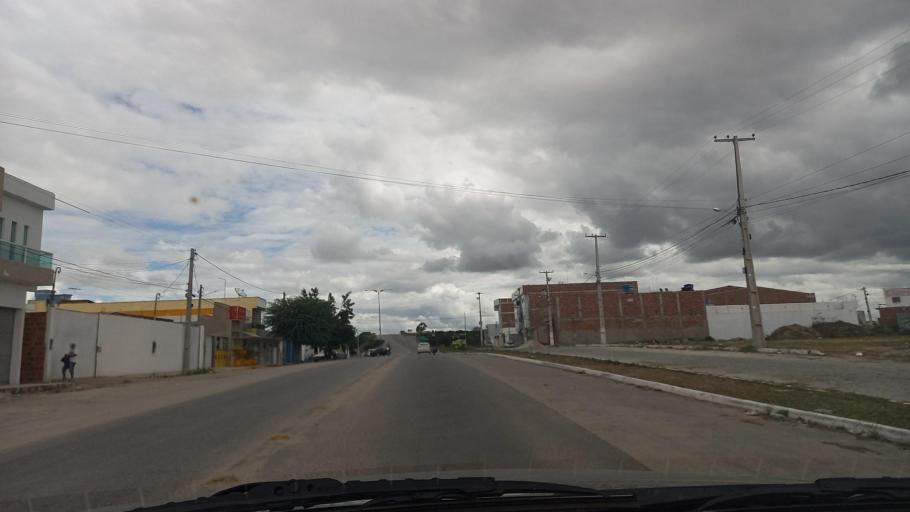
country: BR
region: Pernambuco
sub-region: Caruaru
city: Caruaru
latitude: -8.3269
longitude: -36.1434
